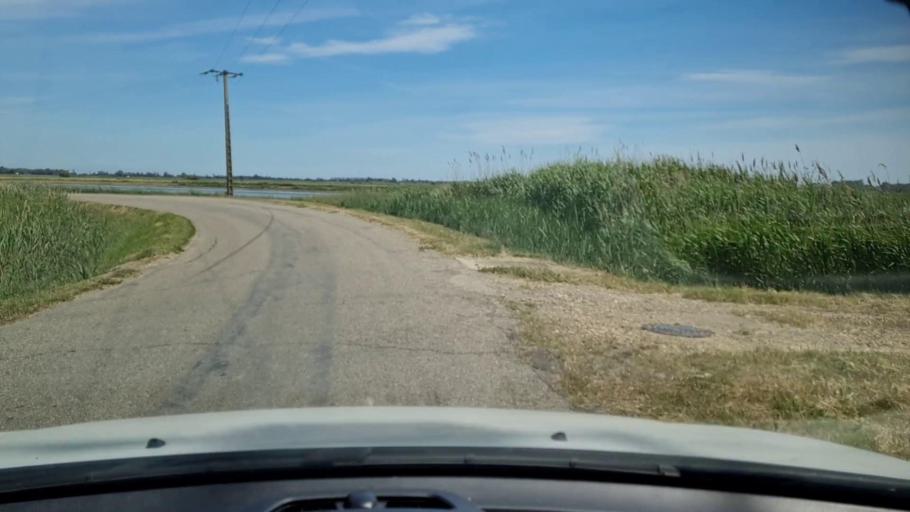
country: FR
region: Languedoc-Roussillon
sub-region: Departement du Gard
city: Saint-Gilles
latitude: 43.6029
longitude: 4.4368
